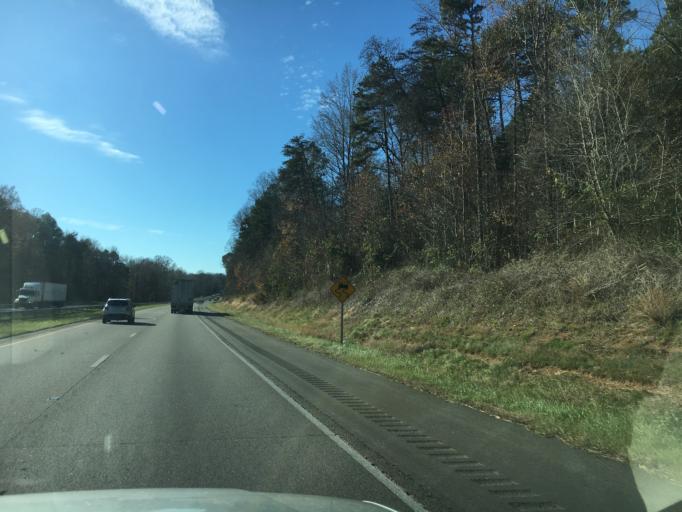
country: US
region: North Carolina
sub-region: Catawba County
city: Claremont
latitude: 35.7300
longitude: -81.1152
